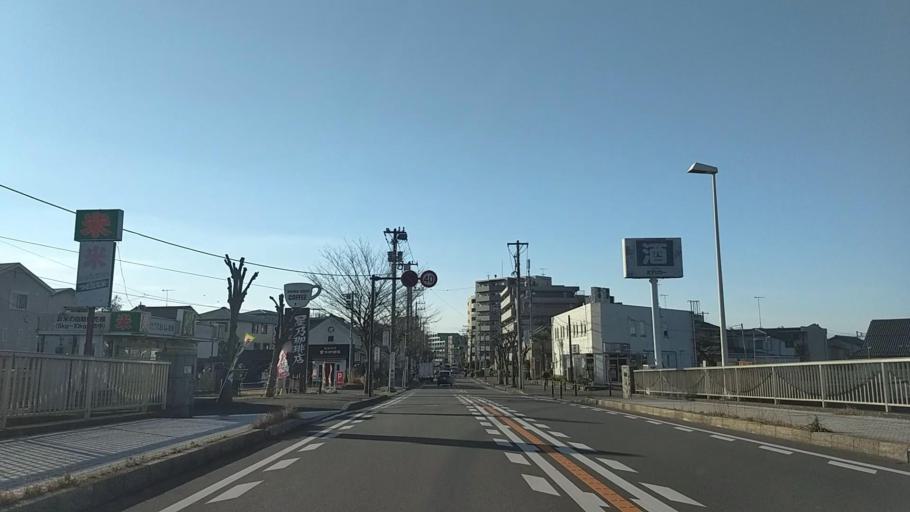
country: JP
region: Kanagawa
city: Fujisawa
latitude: 35.3224
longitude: 139.4863
